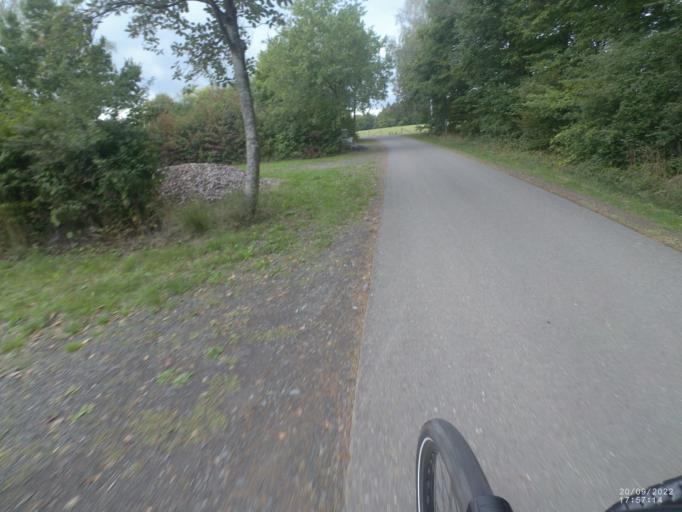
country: DE
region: Rheinland-Pfalz
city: Ellscheid
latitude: 50.1558
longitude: 6.9212
